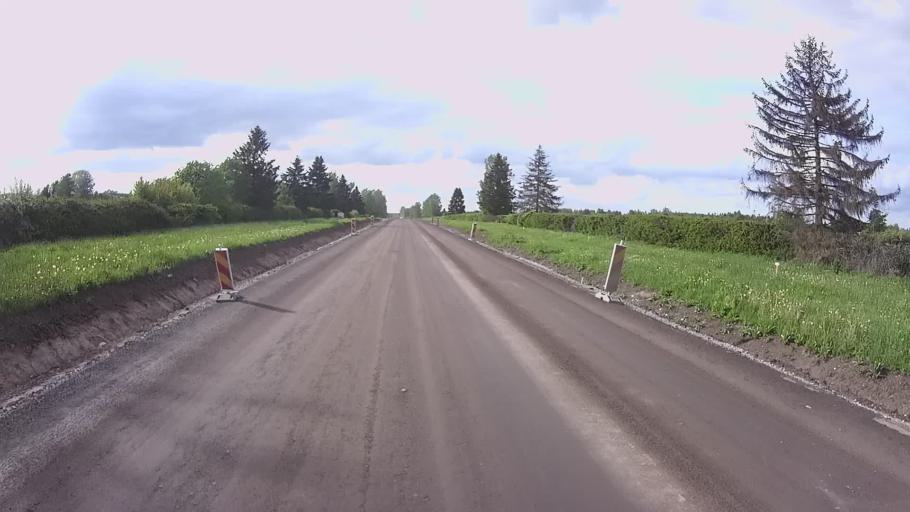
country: EE
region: Jogevamaa
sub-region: Mustvee linn
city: Mustvee
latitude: 59.0197
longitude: 26.7034
